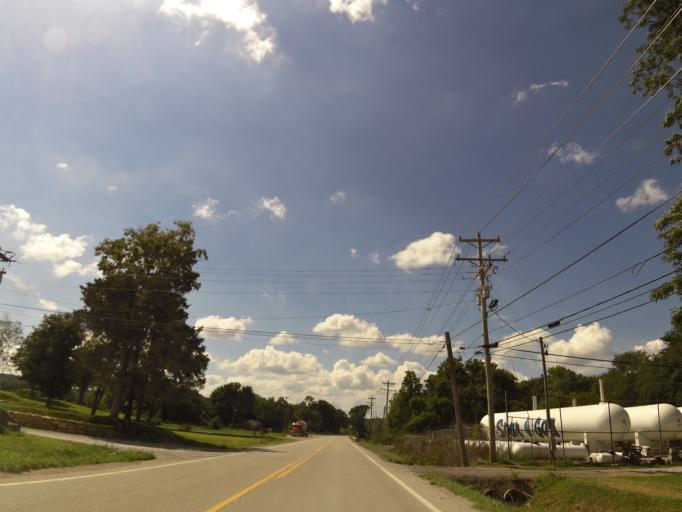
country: US
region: Tennessee
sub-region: Cumberland County
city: Fairfield Glade
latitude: 35.9055
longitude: -84.8707
